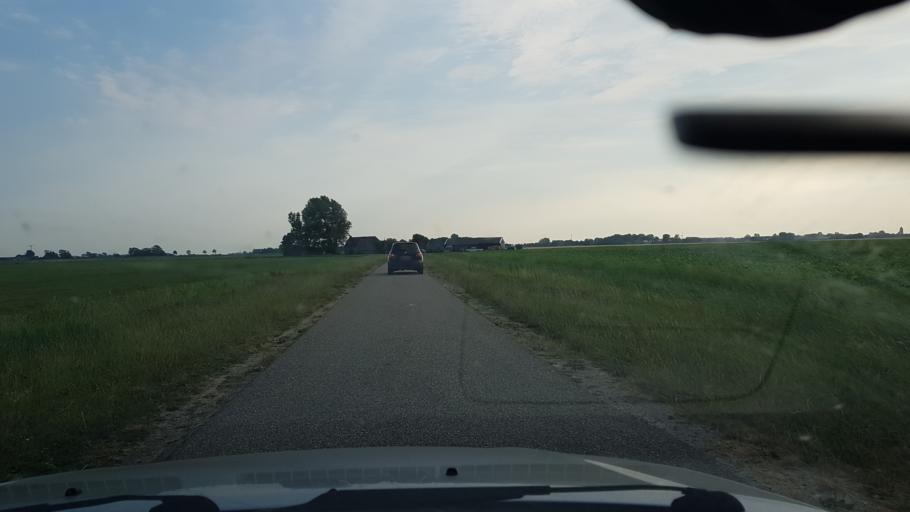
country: NL
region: Friesland
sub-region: Gemeente Dongeradeel
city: Holwerd
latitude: 53.3434
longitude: 5.8704
